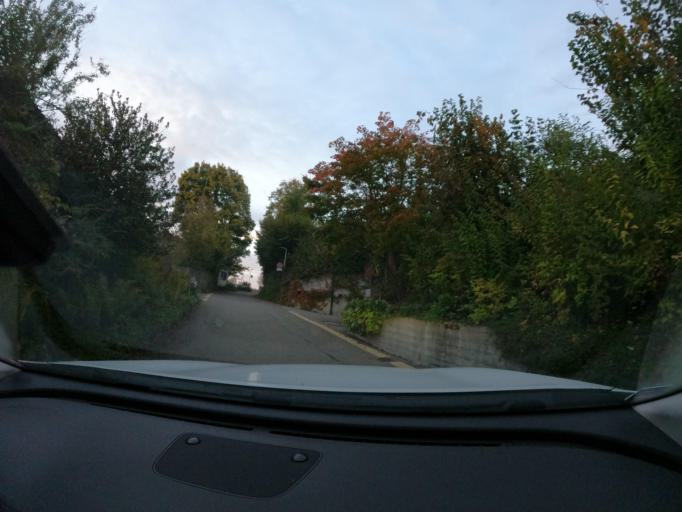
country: CH
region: Bern
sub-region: Bern-Mittelland District
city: Stettlen
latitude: 46.9603
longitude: 7.5278
